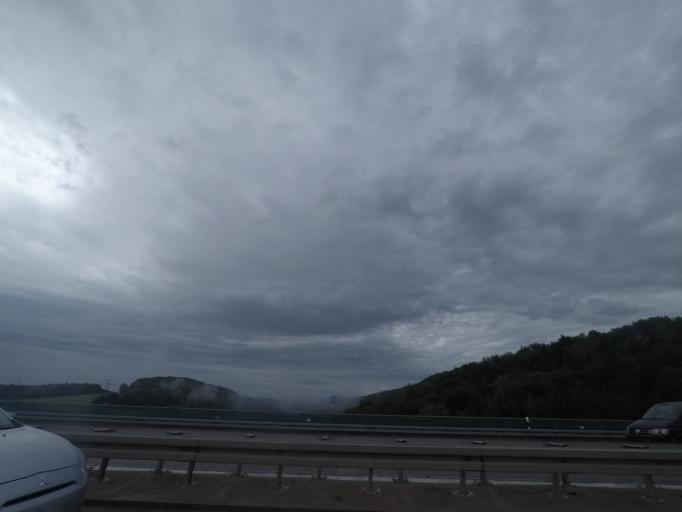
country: DE
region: Baden-Wuerttemberg
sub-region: Freiburg Region
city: Rheinfelden (Baden)
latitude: 47.5875
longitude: 7.7477
